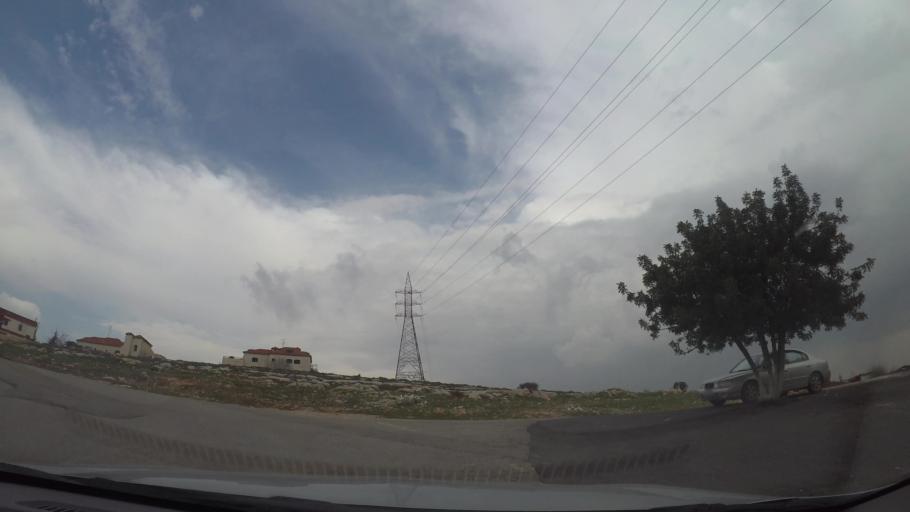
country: JO
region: Amman
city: Umm as Summaq
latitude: 31.8830
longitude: 35.8698
